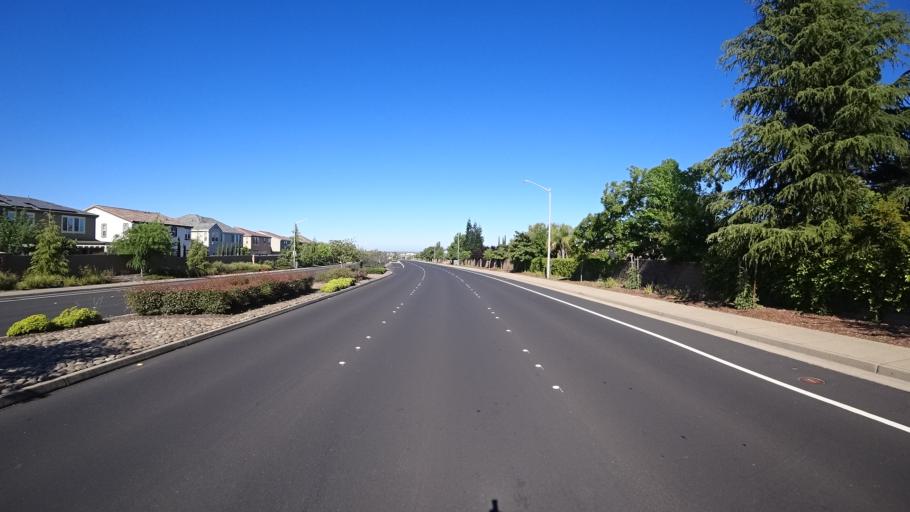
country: US
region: California
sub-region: Placer County
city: Rocklin
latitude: 38.8189
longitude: -121.2758
